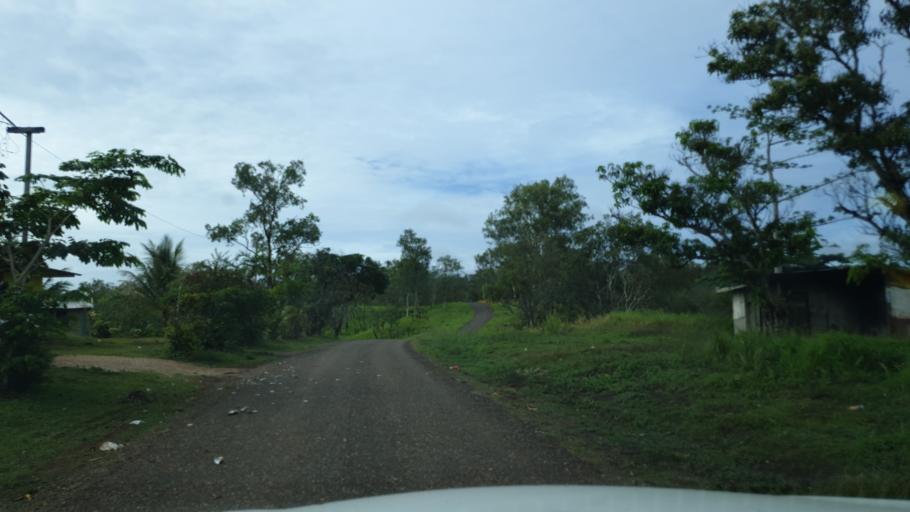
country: PG
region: National Capital
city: Port Moresby
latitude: -9.4300
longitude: 147.3942
